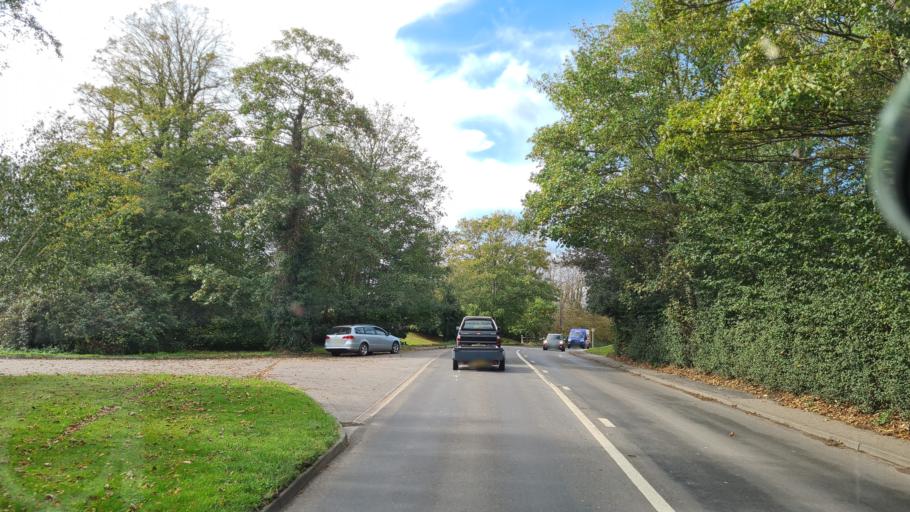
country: GB
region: England
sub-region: East Sussex
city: Bodle Street
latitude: 50.8834
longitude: 0.3492
